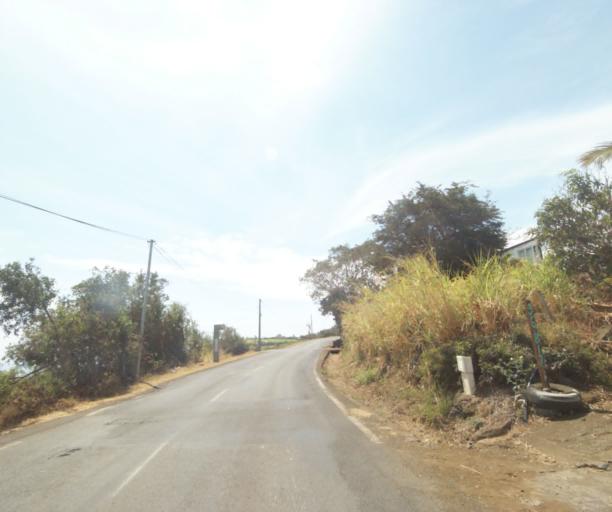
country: RE
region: Reunion
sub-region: Reunion
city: Trois-Bassins
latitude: -21.0972
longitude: 55.2708
